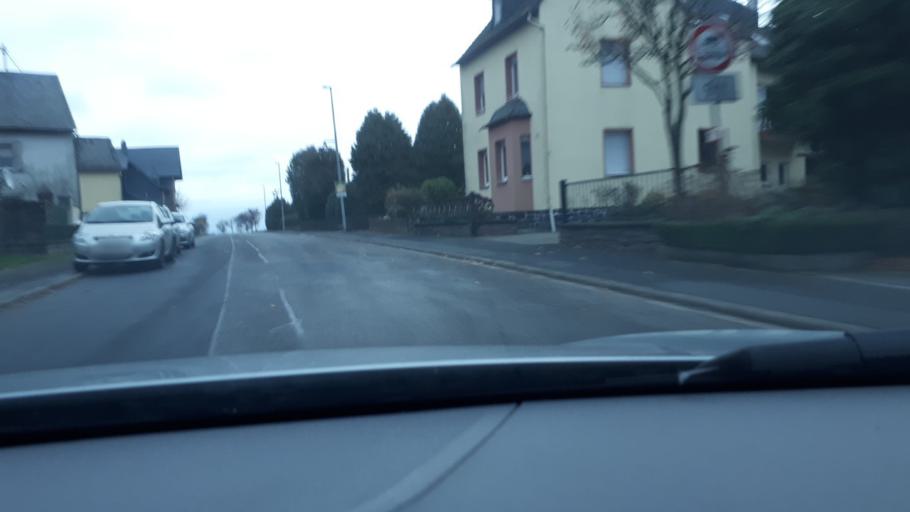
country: DE
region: Rheinland-Pfalz
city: Dungenheim
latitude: 50.2591
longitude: 7.1720
